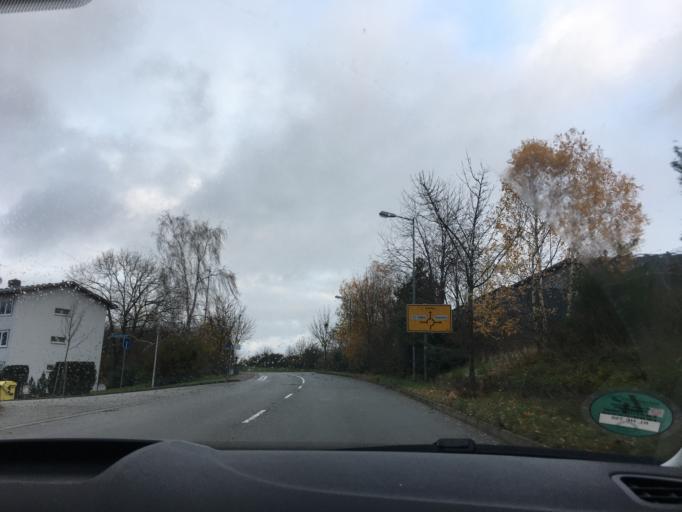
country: DE
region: Rheinland-Pfalz
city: Pirmasens
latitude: 49.2165
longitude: 7.6079
